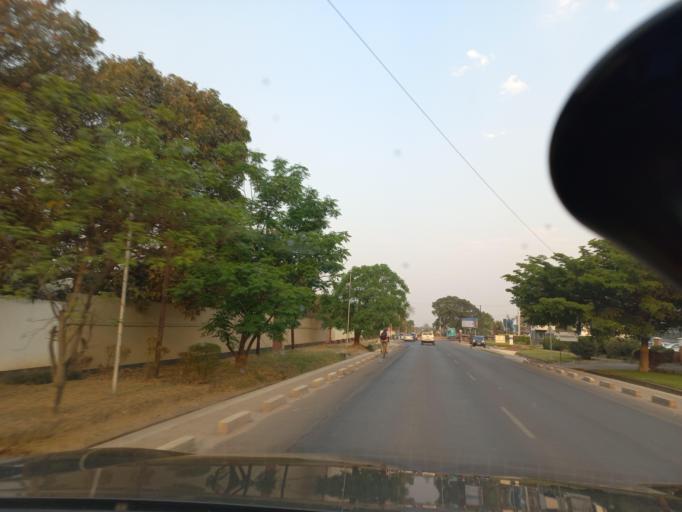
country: ZM
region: Lusaka
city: Lusaka
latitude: -15.3947
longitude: 28.2783
